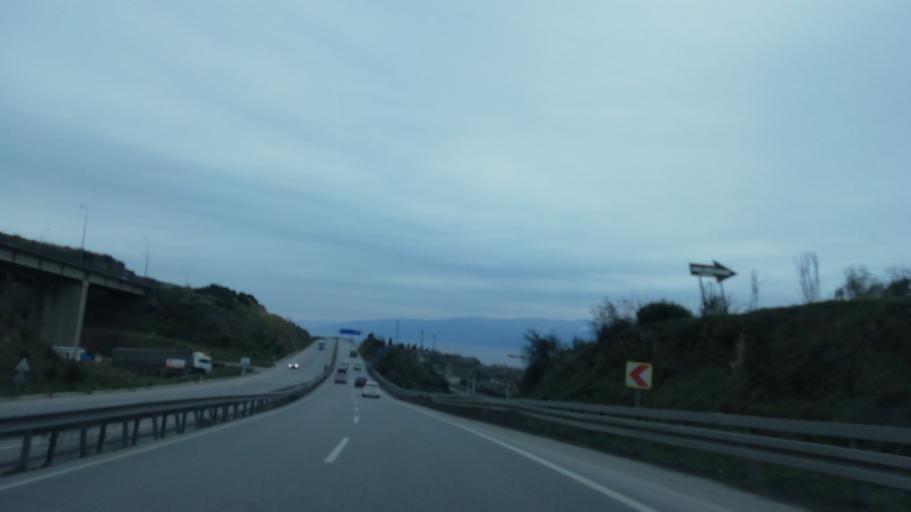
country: TR
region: Kocaeli
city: Tavsancil
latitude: 40.7708
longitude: 29.5622
